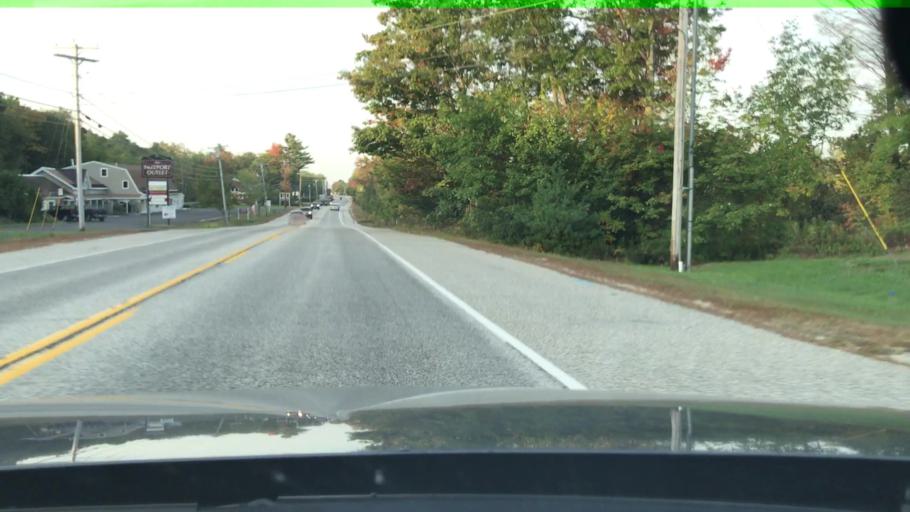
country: US
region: Maine
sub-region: Cumberland County
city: Freeport
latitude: 43.8378
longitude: -70.1241
